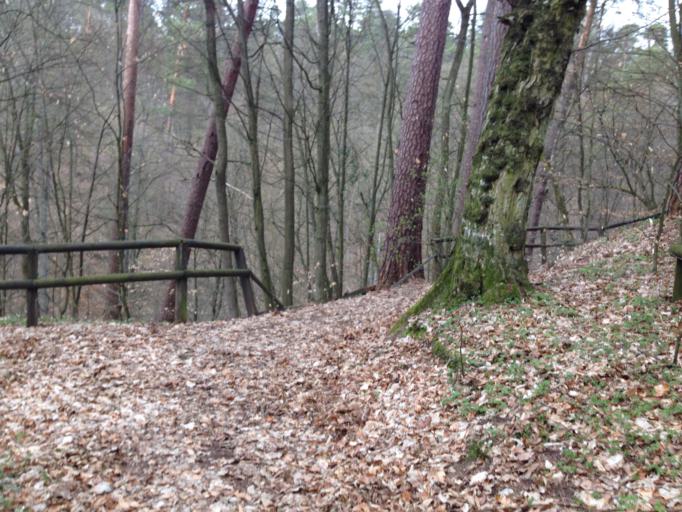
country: PL
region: Kujawsko-Pomorskie
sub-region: Powiat brodnicki
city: Gorzno
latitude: 53.2310
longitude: 19.7200
